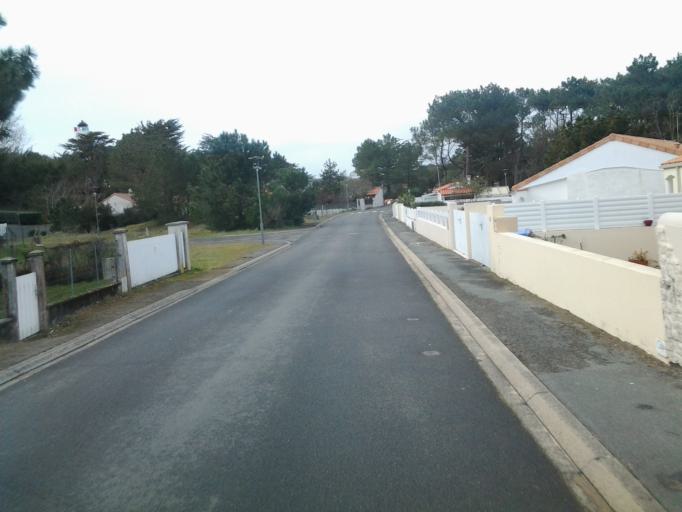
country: FR
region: Pays de la Loire
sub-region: Departement de la Vendee
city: La Tranche-sur-Mer
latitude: 46.3441
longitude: -1.4613
